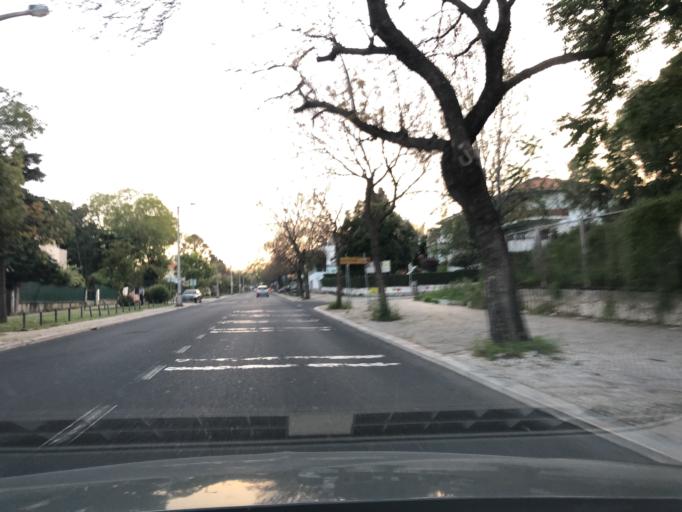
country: PT
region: Lisbon
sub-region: Oeiras
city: Alges
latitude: 38.7008
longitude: -9.2086
